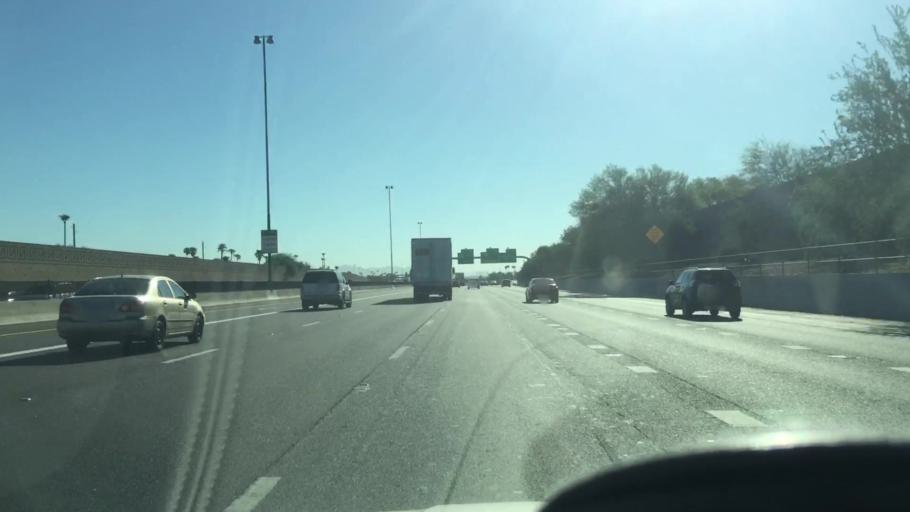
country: US
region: Arizona
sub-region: Maricopa County
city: Tempe
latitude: 33.3877
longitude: -111.9185
